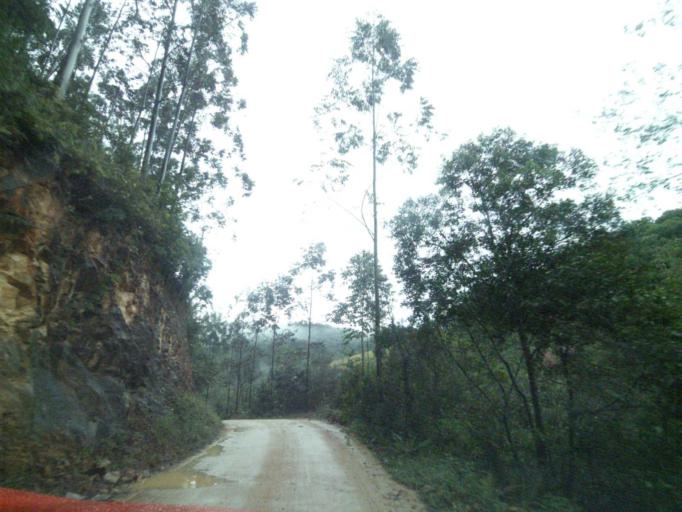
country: BR
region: Santa Catarina
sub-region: Anitapolis
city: Anitapolis
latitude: -27.9162
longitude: -49.1923
